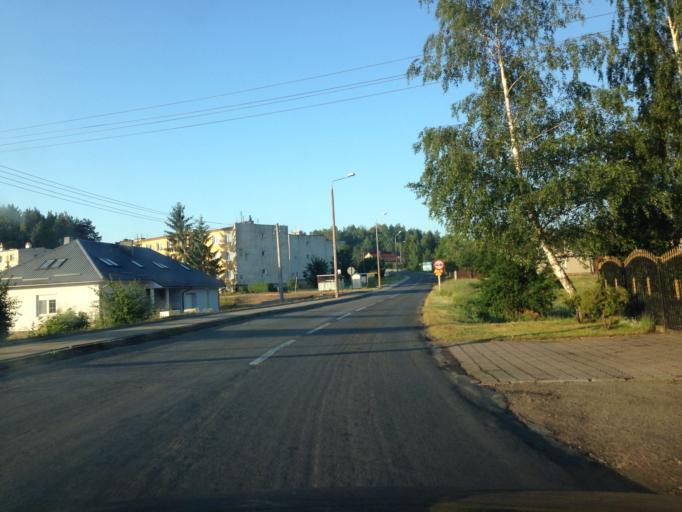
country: PL
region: Pomeranian Voivodeship
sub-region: Powiat tczewski
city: Gniew
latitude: 53.8214
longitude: 18.8169
